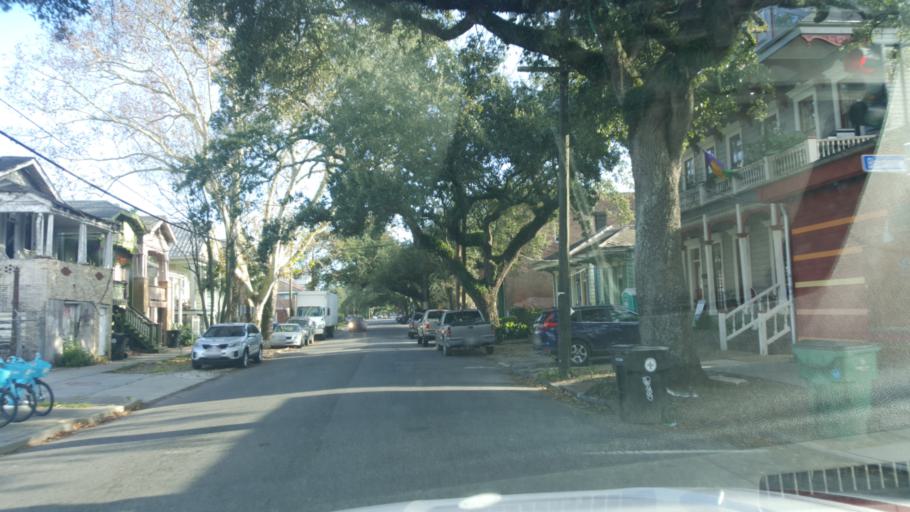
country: US
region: Louisiana
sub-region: Orleans Parish
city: New Orleans
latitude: 29.9328
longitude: -90.0873
